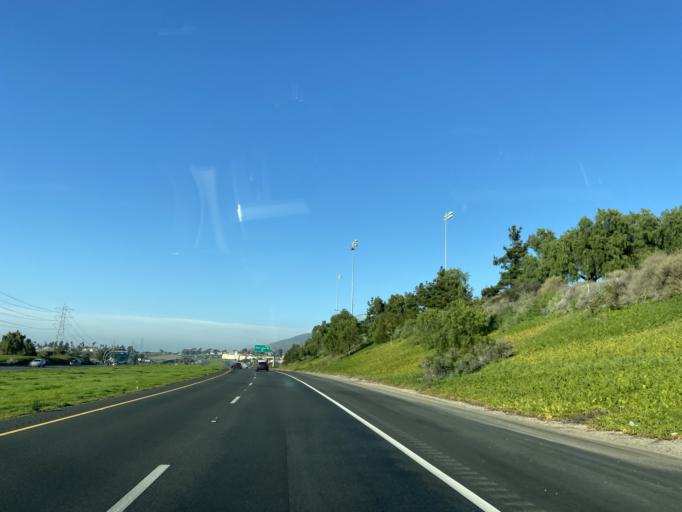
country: US
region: California
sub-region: San Diego County
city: Bonita
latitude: 32.6396
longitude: -116.9705
